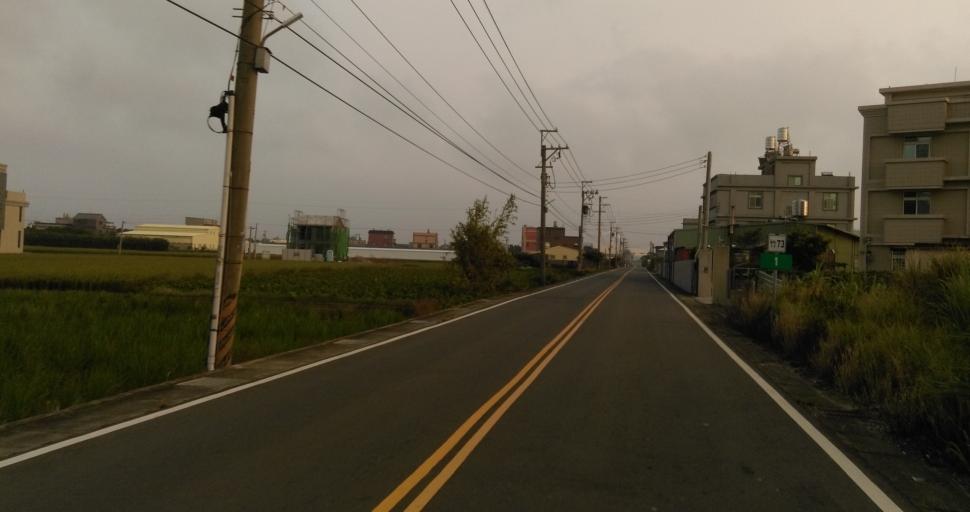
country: TW
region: Taiwan
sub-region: Hsinchu
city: Zhubei
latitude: 24.8686
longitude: 120.9586
